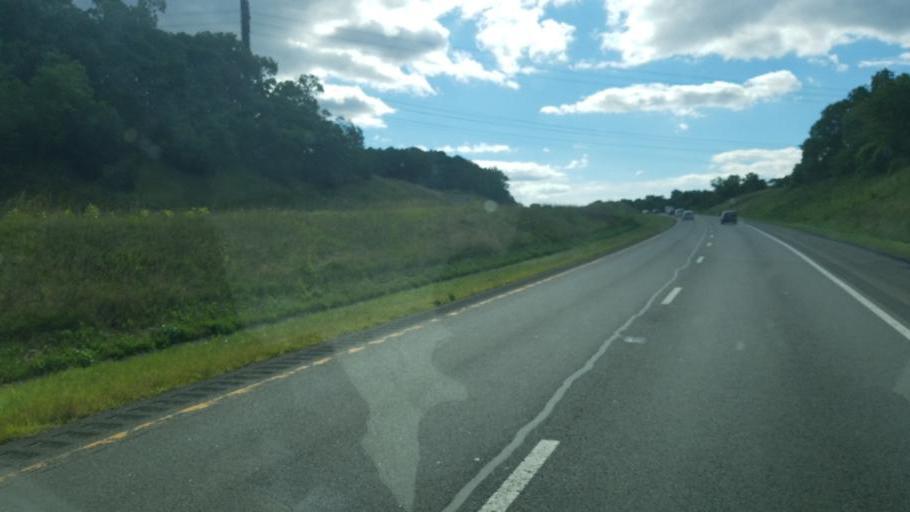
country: US
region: Virginia
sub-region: Warren County
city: Front Royal
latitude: 38.9537
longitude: -78.1823
